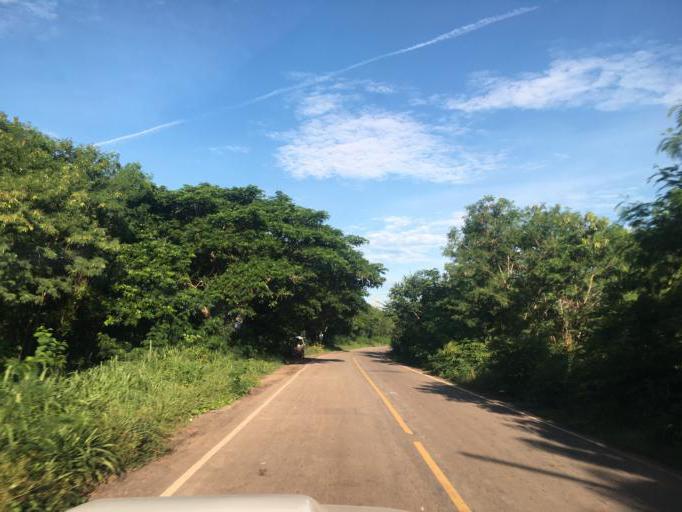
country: TH
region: Changwat Udon Thani
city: Kut Chap
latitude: 17.3803
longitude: 102.6038
